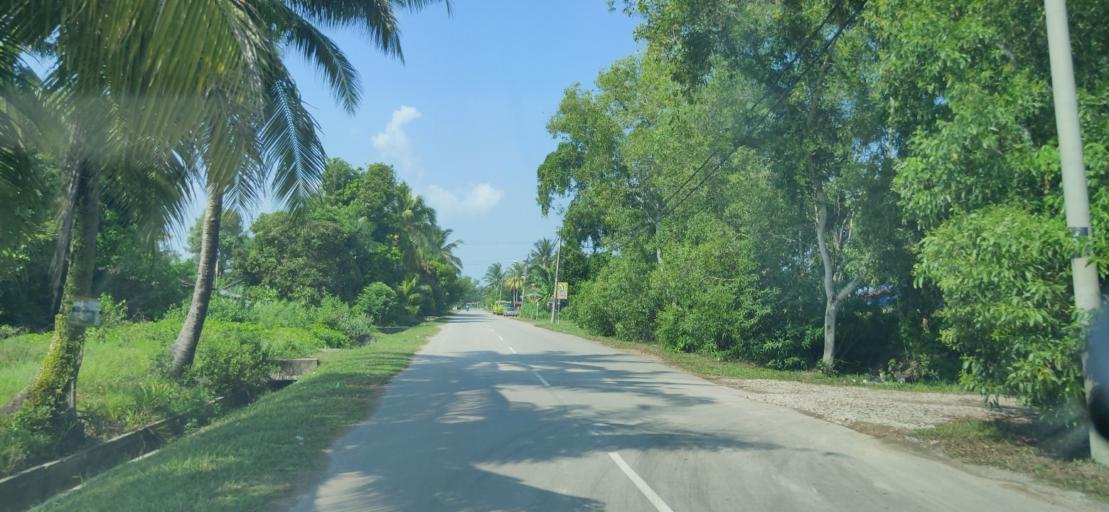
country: MY
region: Kedah
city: Sungai Petani
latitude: 5.6645
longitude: 100.4606
